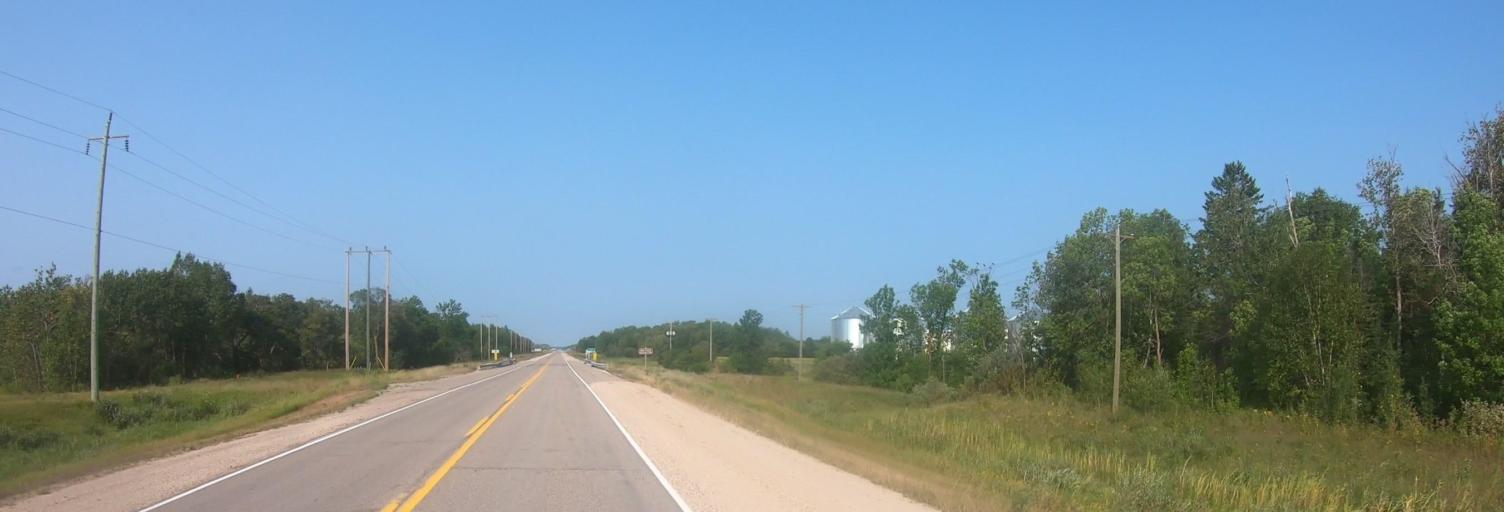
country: US
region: Minnesota
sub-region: Roseau County
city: Roseau
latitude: 49.0234
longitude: -95.6266
